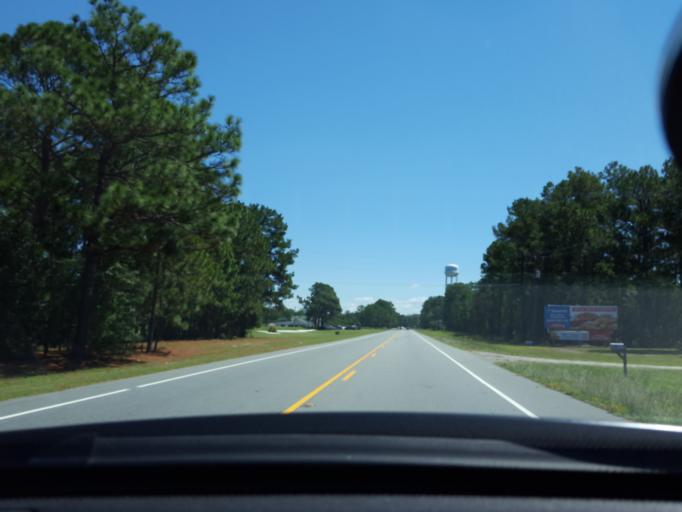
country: US
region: North Carolina
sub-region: Bladen County
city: Elizabethtown
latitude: 34.6499
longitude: -78.5384
